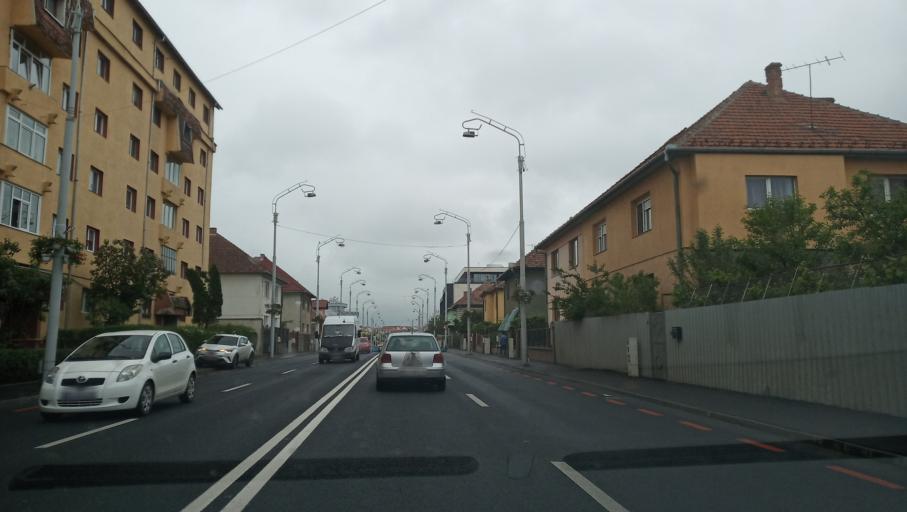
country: RO
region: Sibiu
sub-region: Municipiul Sibiu
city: Sibiu
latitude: 45.7922
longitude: 24.1372
